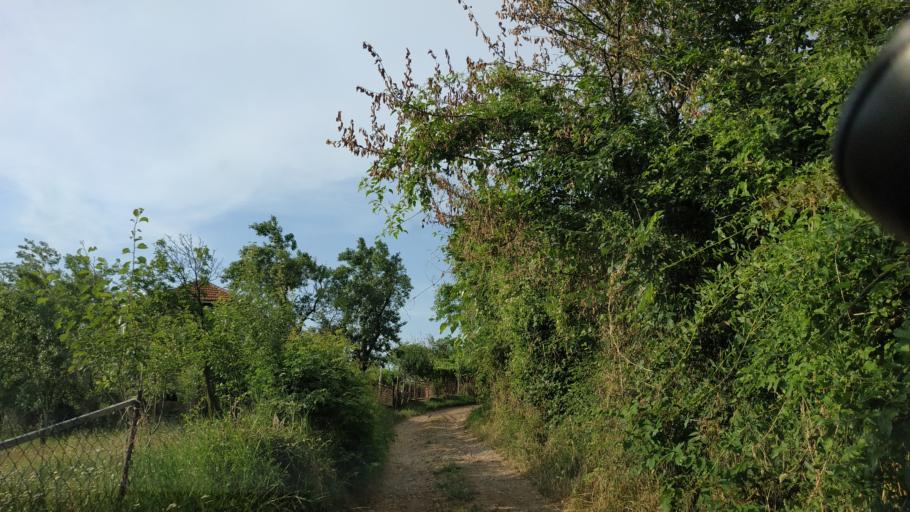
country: RS
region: Central Serbia
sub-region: Nisavski Okrug
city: Aleksinac
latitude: 43.6073
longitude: 21.6933
